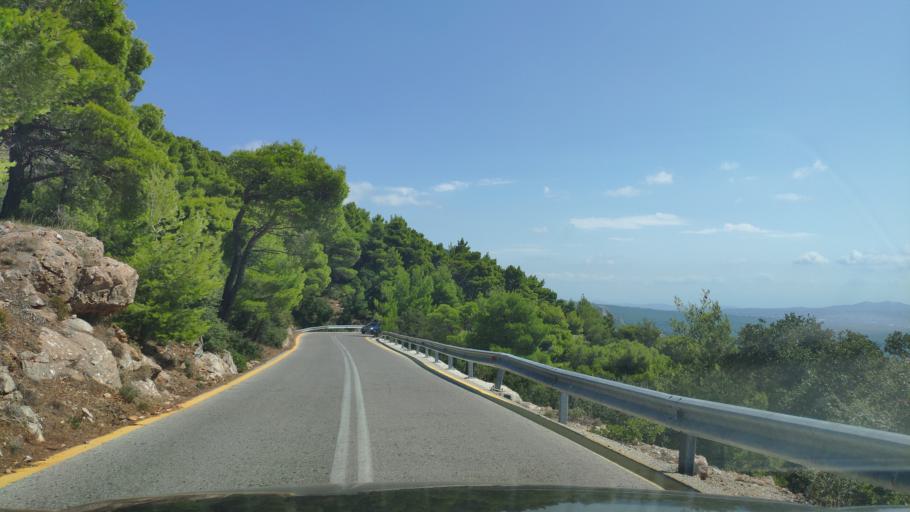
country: GR
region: Attica
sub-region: Nomarchia Anatolikis Attikis
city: Thrakomakedones
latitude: 38.1384
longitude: 23.7229
